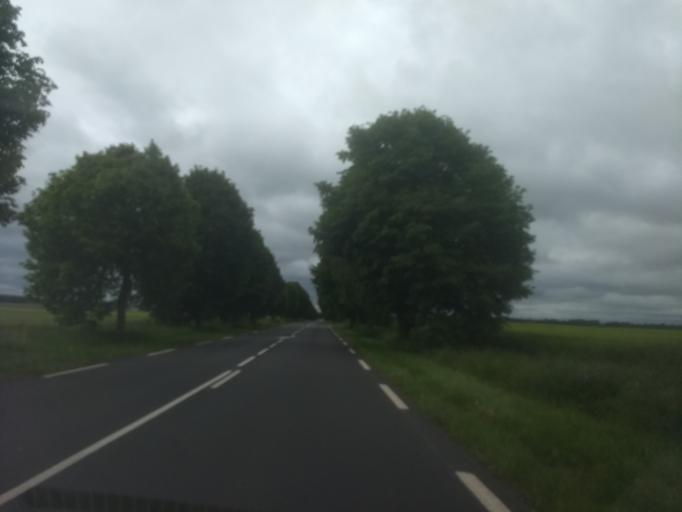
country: FR
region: Centre
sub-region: Departement d'Eure-et-Loir
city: Treon
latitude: 48.6581
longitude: 1.3022
